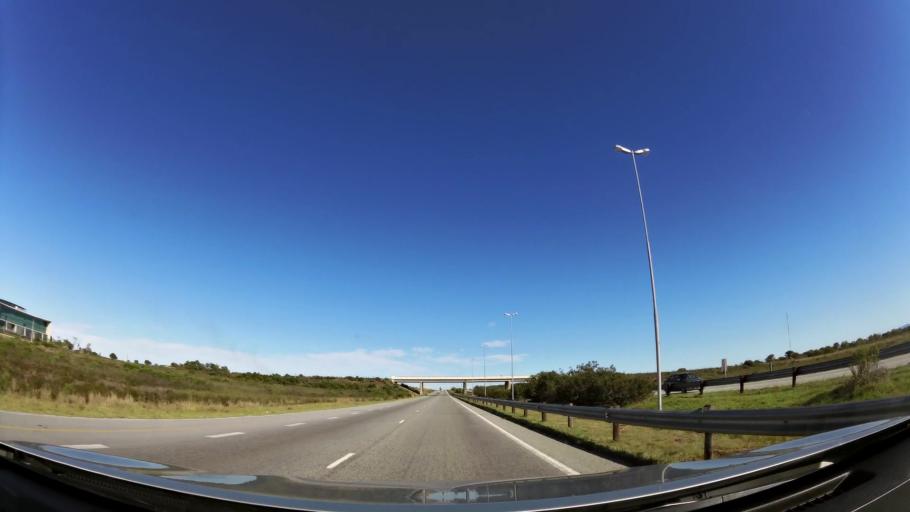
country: ZA
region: Eastern Cape
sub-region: Nelson Mandela Bay Metropolitan Municipality
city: Port Elizabeth
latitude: -33.9478
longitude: 25.4582
